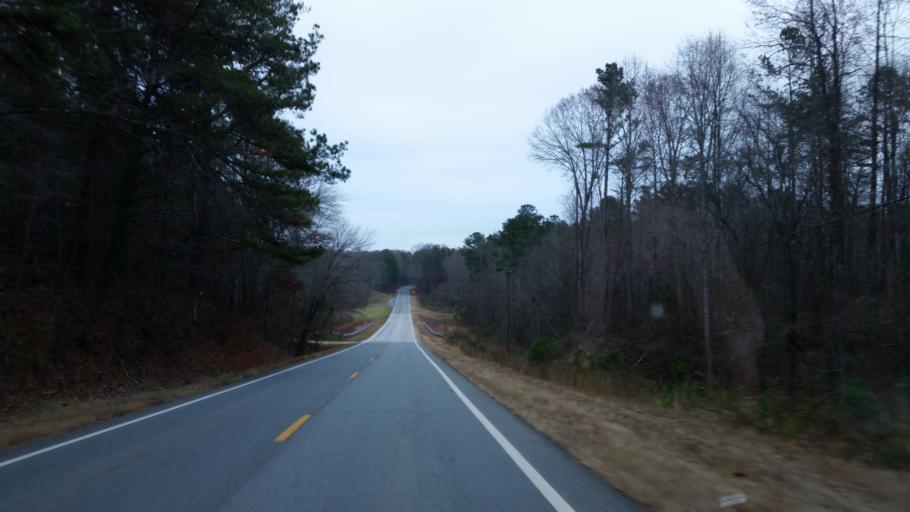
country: US
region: Georgia
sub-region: Dawson County
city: Dawsonville
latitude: 34.4464
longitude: -84.1120
